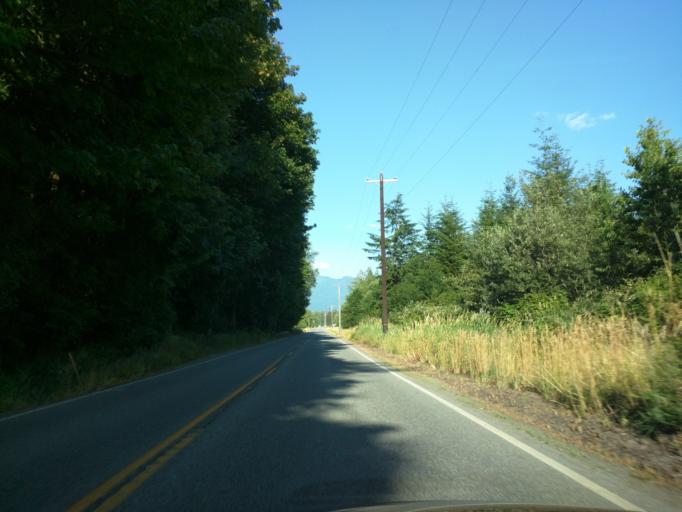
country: US
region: Washington
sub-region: Snohomish County
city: Darrington
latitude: 48.2692
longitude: -121.6883
